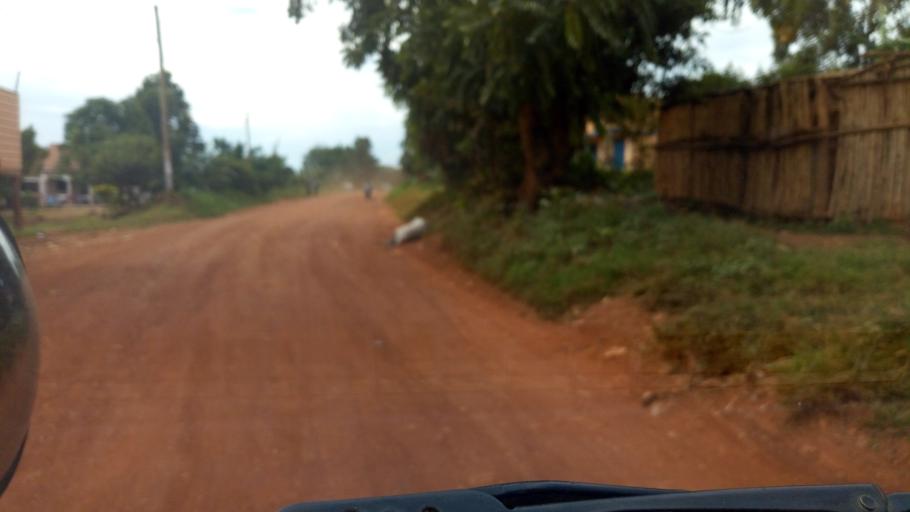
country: UG
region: Central Region
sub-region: Wakiso District
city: Bweyogerere
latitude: 0.3535
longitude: 32.7002
